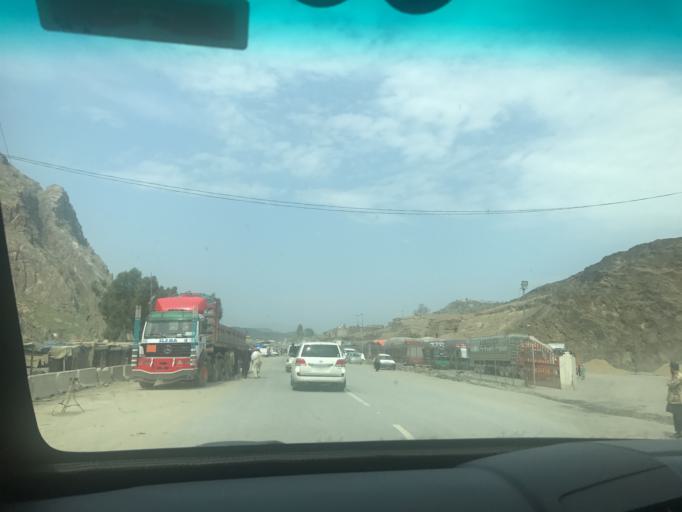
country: PK
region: Federally Administered Tribal Areas
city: Landi Kotal
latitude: 34.1176
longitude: 71.1006
